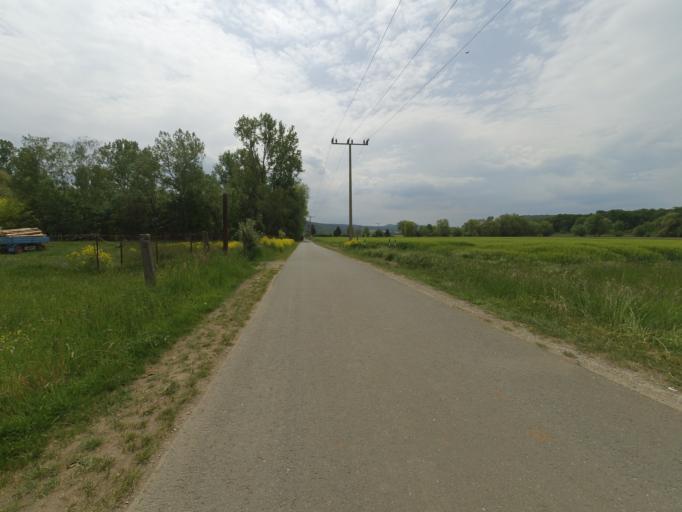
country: DE
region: Thuringia
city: Sulza
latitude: 50.8642
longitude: 11.6080
